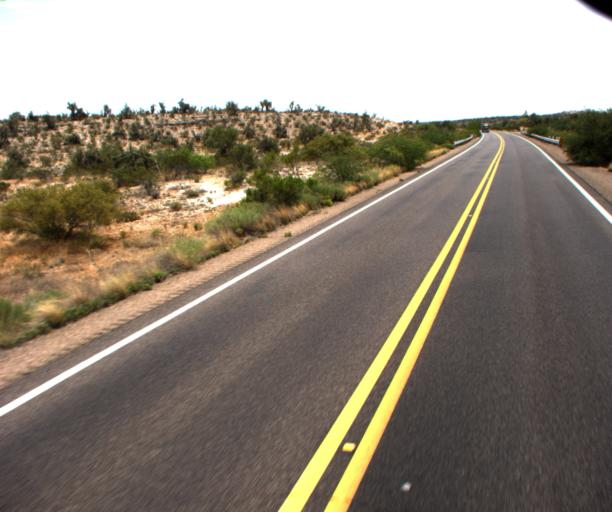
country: US
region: Arizona
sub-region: Gila County
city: Peridot
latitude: 33.2744
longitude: -110.3268
